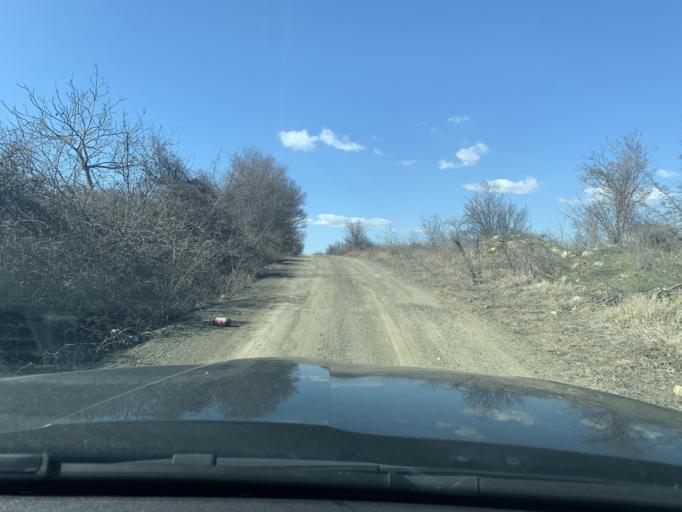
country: MK
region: Demir Kapija
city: Demir Kapija
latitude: 41.4135
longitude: 22.2224
